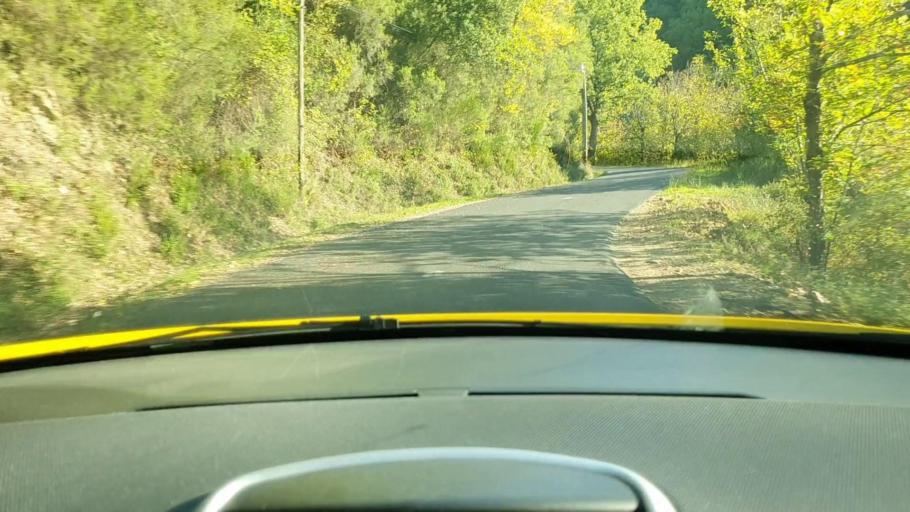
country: FR
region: Languedoc-Roussillon
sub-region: Departement du Gard
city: Sumene
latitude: 43.9852
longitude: 3.7427
